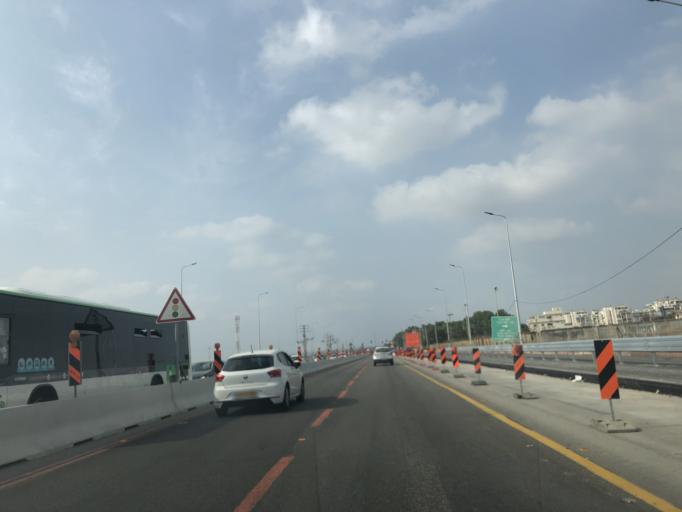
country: IL
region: Central District
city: Rosh Ha'Ayin
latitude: 32.0907
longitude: 34.9431
